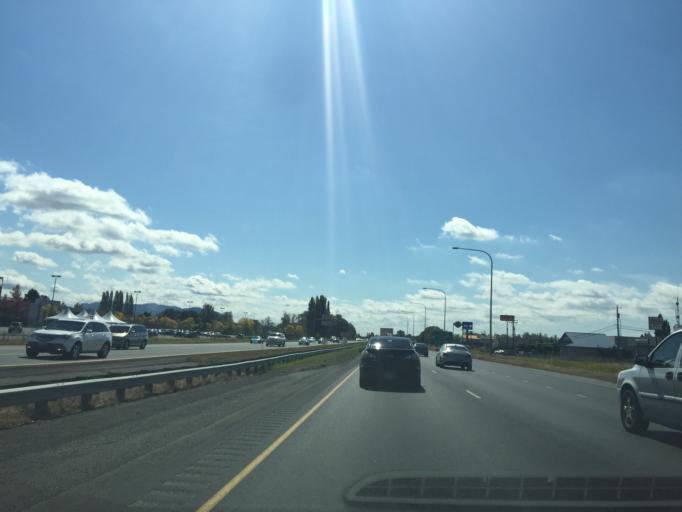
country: US
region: Washington
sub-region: Skagit County
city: Burlington
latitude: 48.4638
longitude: -122.3416
